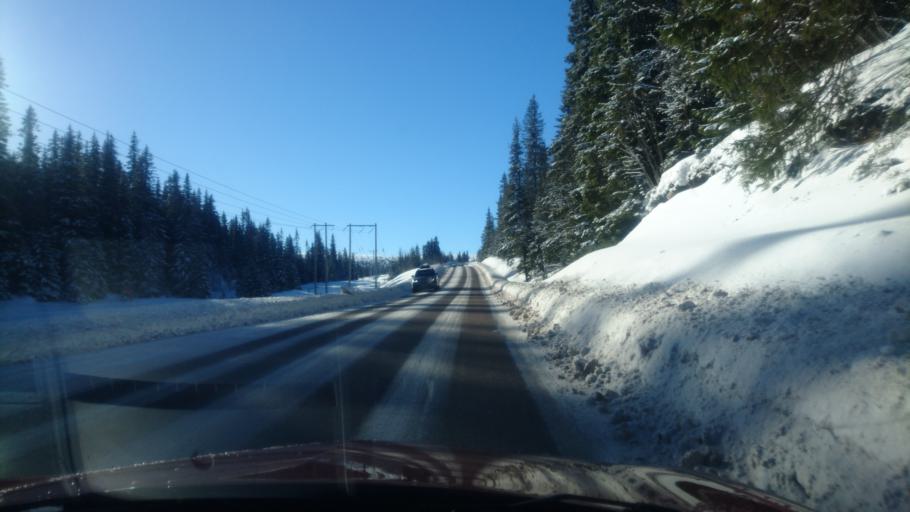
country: SE
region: Dalarna
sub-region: Malung-Saelens kommun
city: Malung
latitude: 61.1645
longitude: 13.1468
